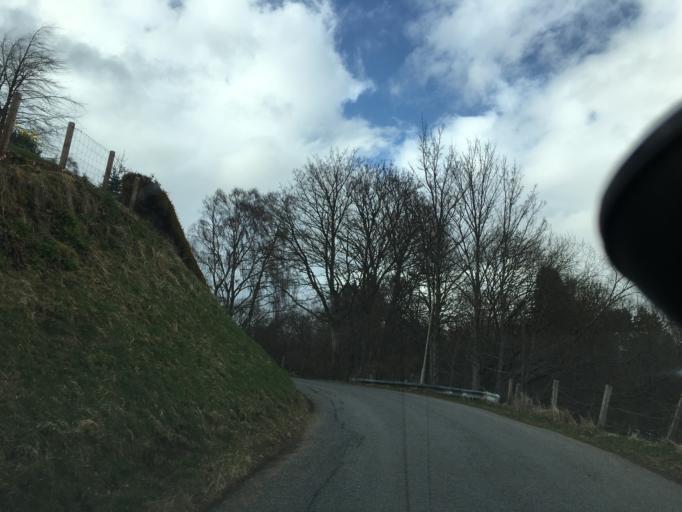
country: GB
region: Scotland
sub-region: Highland
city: Kingussie
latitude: 57.0819
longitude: -4.0537
